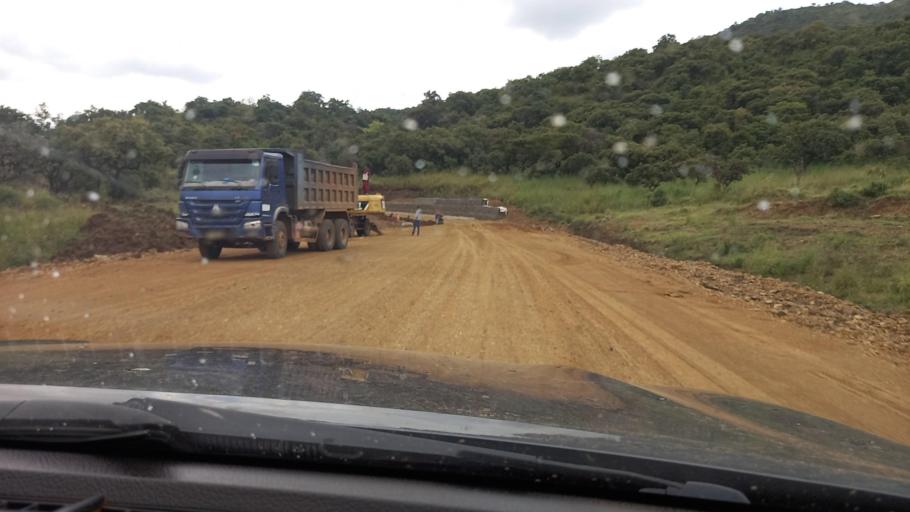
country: ET
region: Southern Nations, Nationalities, and People's Region
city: Mizan Teferi
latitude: 6.2085
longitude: 35.6695
